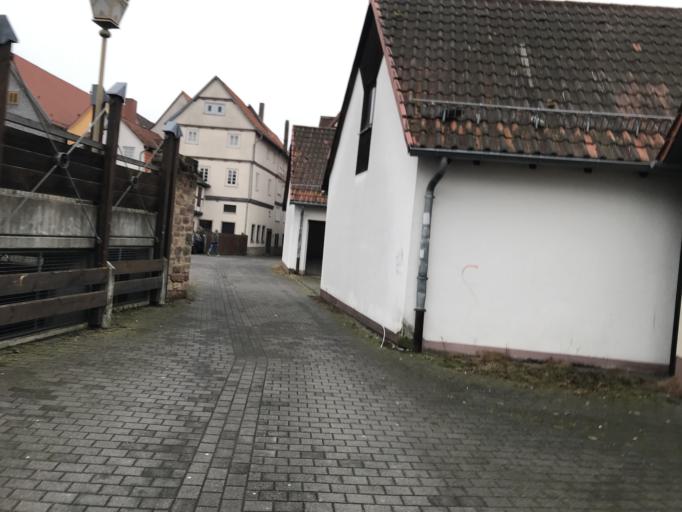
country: DE
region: Hesse
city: Fritzlar
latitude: 51.1325
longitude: 9.2729
